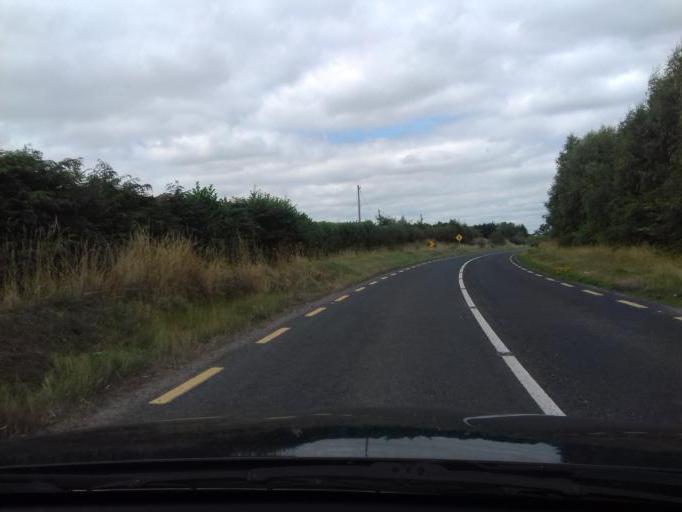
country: IE
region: Leinster
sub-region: County Carlow
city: Tullow
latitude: 52.7866
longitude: -6.7545
